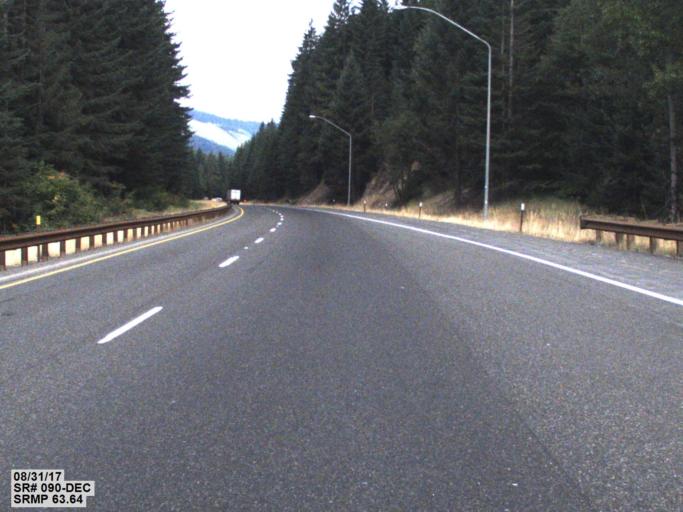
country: US
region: Washington
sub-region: Kittitas County
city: Cle Elum
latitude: 47.3004
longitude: -121.2940
